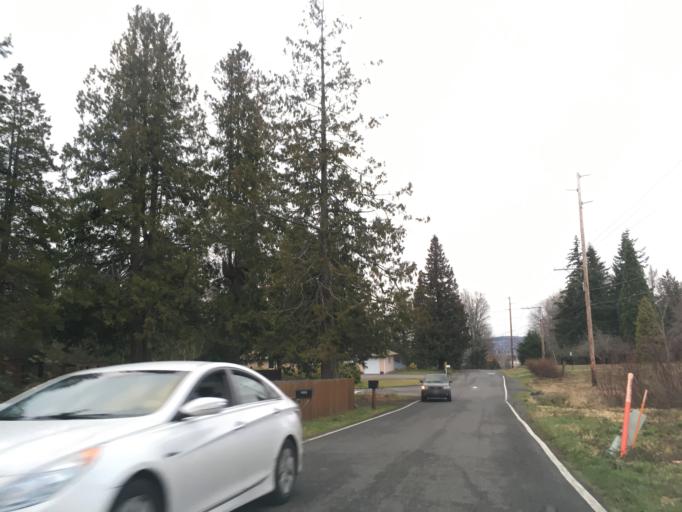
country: US
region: Washington
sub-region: Whatcom County
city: Bellingham
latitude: 48.7303
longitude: -122.4645
